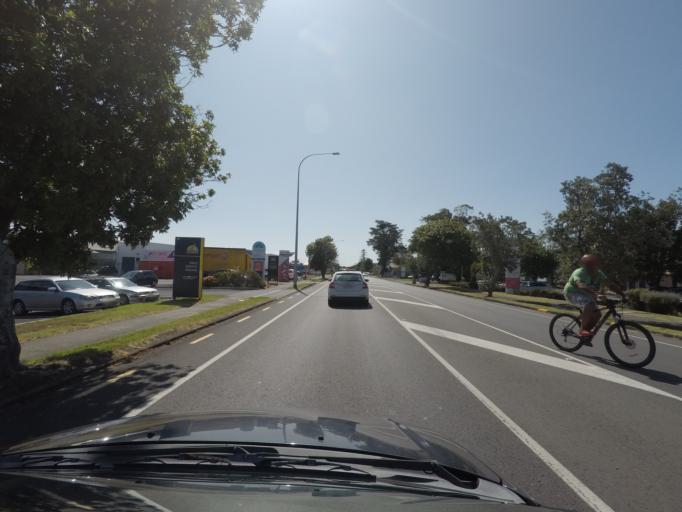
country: NZ
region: Auckland
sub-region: Auckland
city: Rosebank
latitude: -36.8828
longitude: 174.6795
